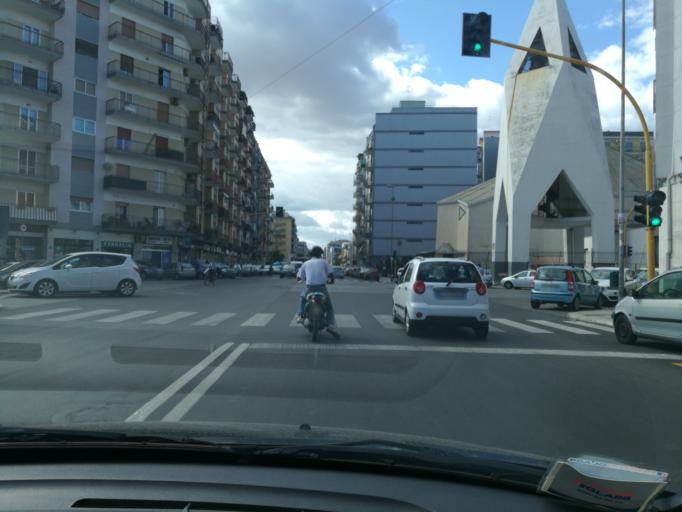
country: IT
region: Apulia
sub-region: Provincia di Bari
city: Bari
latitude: 41.1275
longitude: 16.8515
